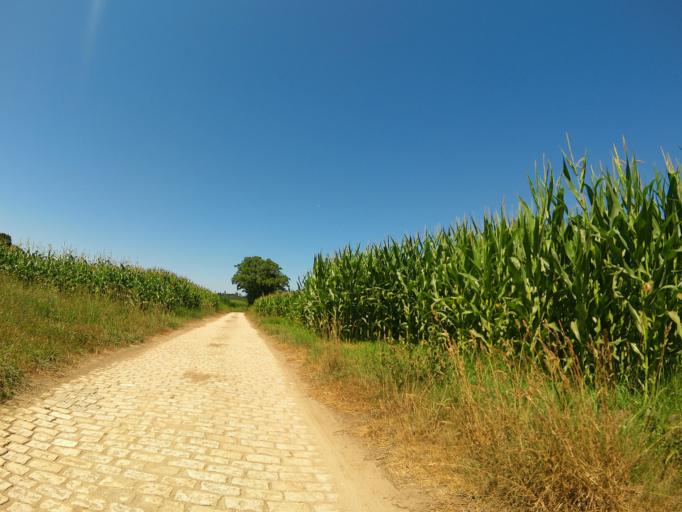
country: PT
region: Viana do Castelo
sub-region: Viana do Castelo
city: Darque
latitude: 41.7250
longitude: -8.6921
